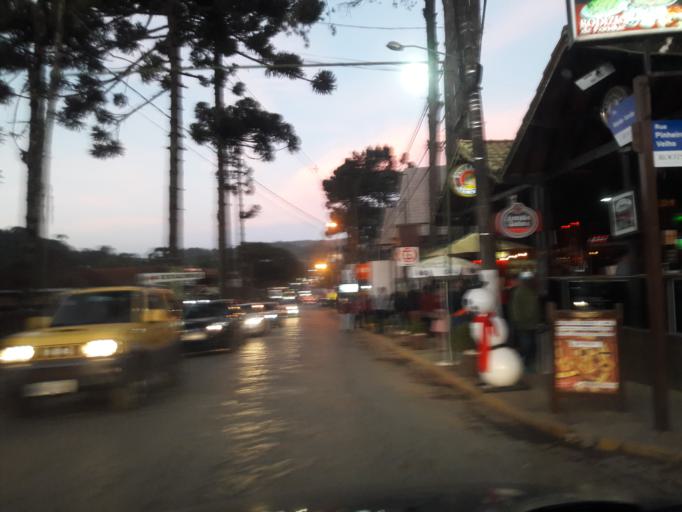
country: BR
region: Minas Gerais
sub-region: Camanducaia
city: Camanducaia
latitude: -22.8634
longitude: -46.0393
